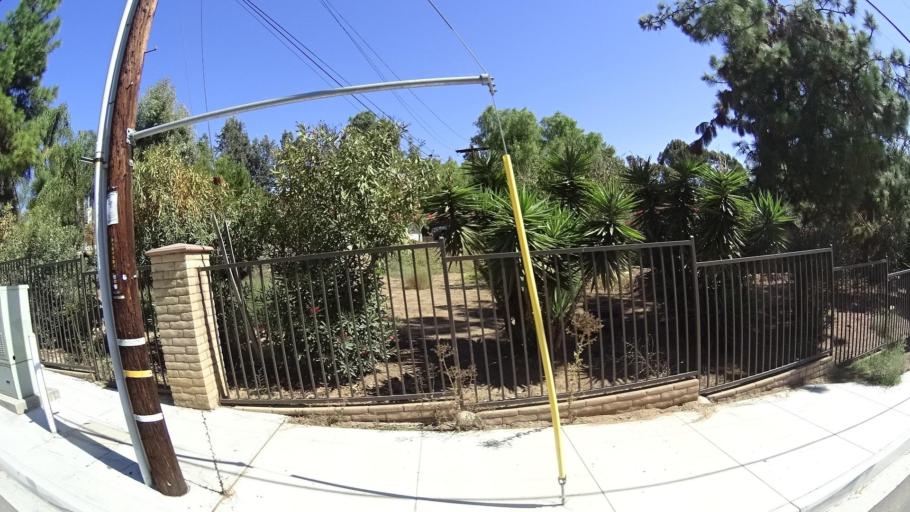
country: US
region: California
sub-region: San Diego County
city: Bonita
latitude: 32.6621
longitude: -117.0489
